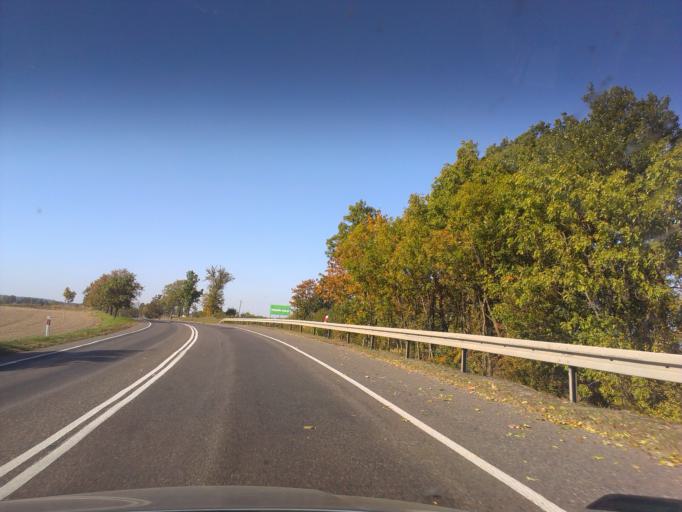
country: PL
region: Greater Poland Voivodeship
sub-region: Powiat chodzieski
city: Budzyn
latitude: 52.9426
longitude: 16.9606
